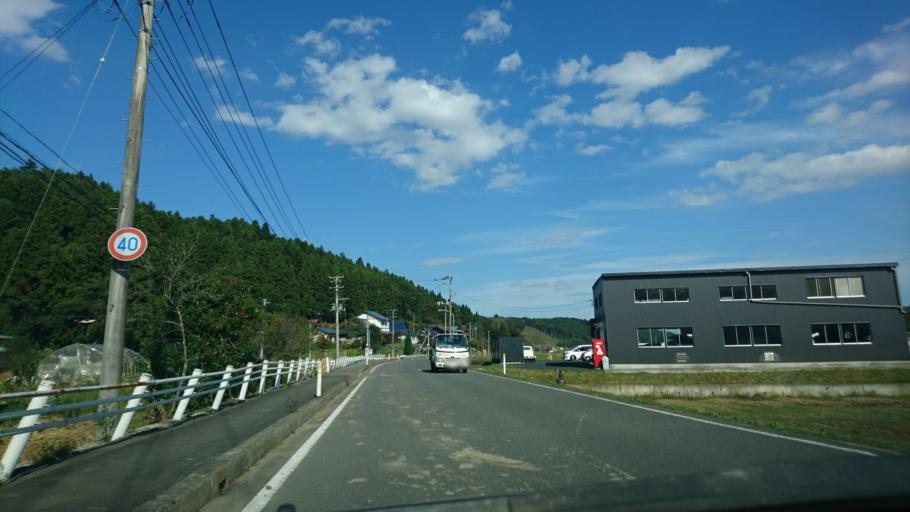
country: JP
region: Iwate
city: Ichinoseki
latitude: 38.8706
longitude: 141.0960
